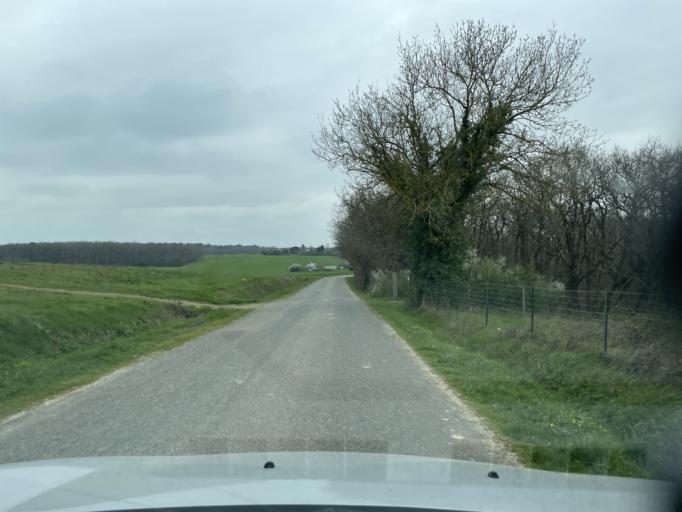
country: FR
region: Midi-Pyrenees
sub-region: Departement du Gers
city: Pujaudran
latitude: 43.6131
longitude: 1.1671
